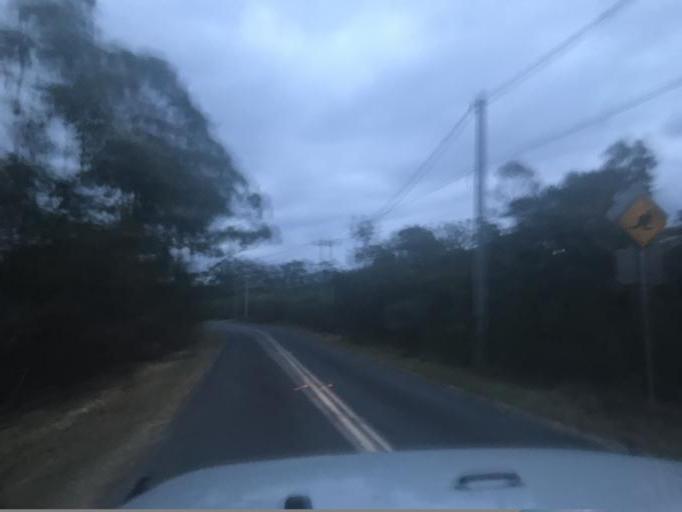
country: AU
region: New South Wales
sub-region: Hawkesbury
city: Pitt Town
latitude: -33.4735
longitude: 150.8635
